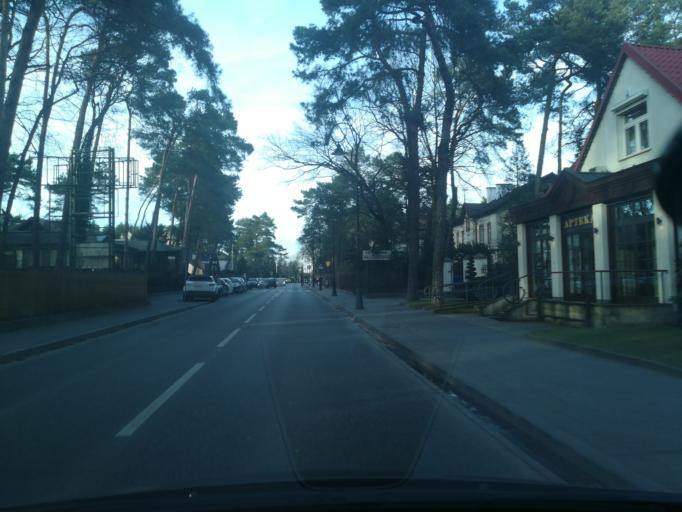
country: PL
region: Masovian Voivodeship
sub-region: Powiat piaseczynski
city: Konstancin-Jeziorna
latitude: 52.0856
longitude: 21.1204
